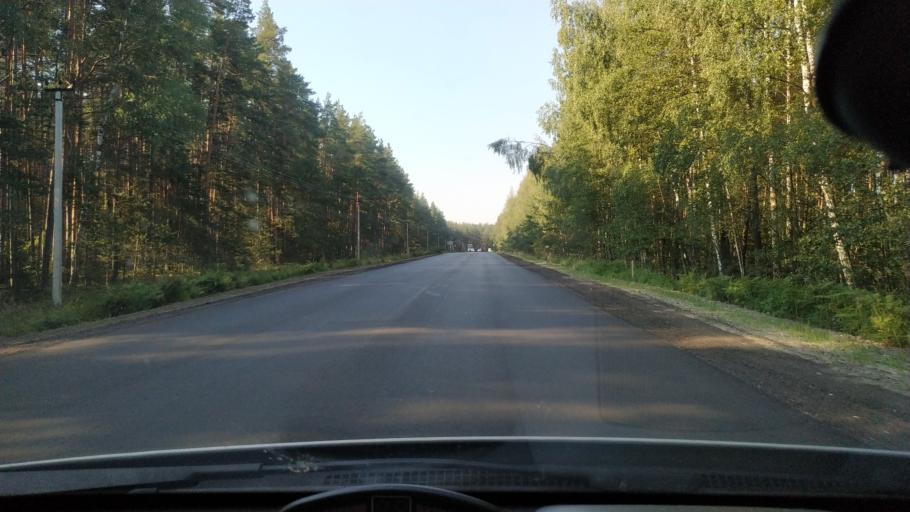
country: RU
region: Moskovskaya
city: Misheronskiy
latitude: 55.6306
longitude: 39.7427
